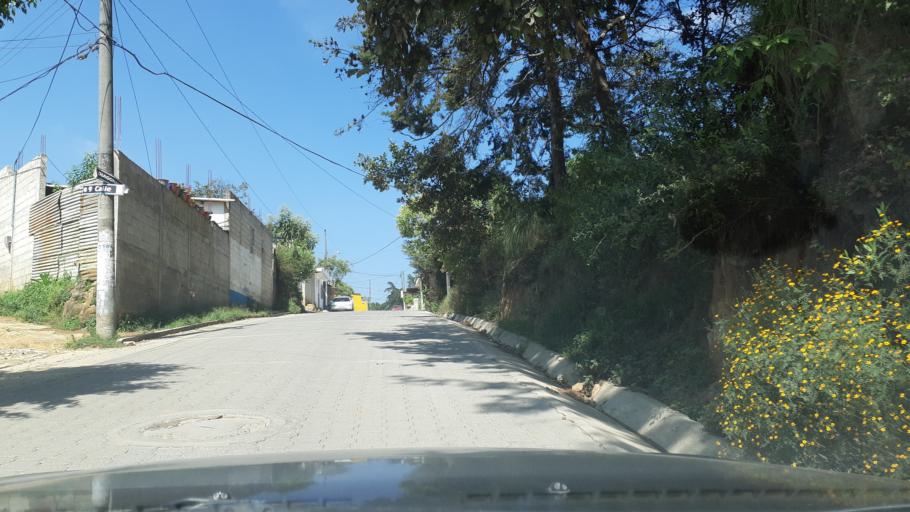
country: GT
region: Chimaltenango
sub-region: Municipio de Chimaltenango
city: Chimaltenango
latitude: 14.6719
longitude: -90.8402
